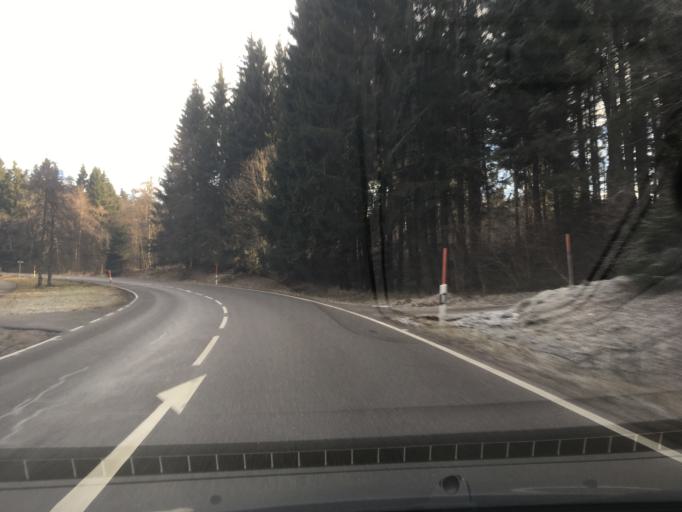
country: DE
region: Baden-Wuerttemberg
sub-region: Freiburg Region
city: Hausern
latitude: 47.7421
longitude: 8.1690
